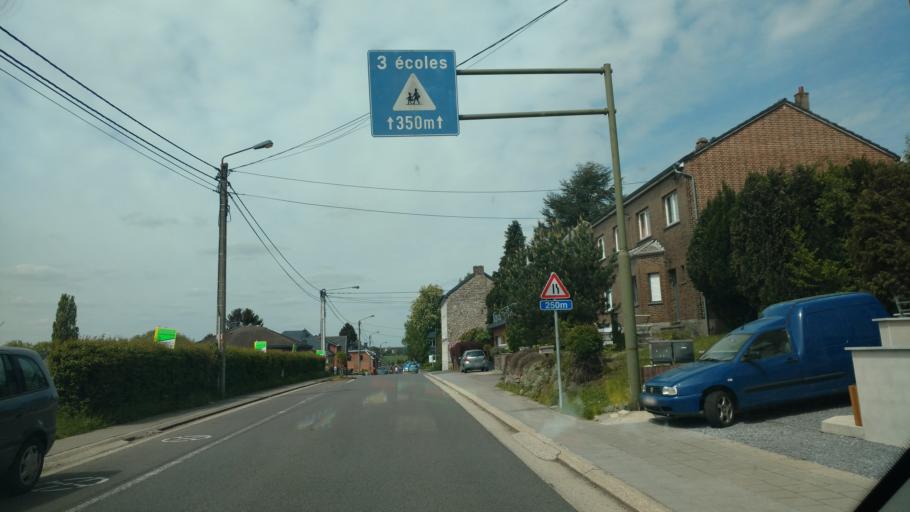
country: BE
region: Wallonia
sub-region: Province de Liege
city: La Calamine
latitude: 50.7335
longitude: 5.9924
